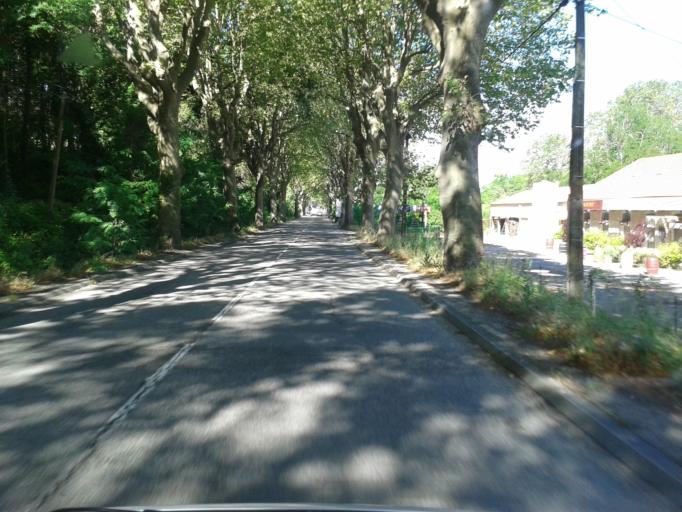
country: FR
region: Provence-Alpes-Cote d'Azur
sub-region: Departement des Bouches-du-Rhone
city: Meyrargues
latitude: 43.6431
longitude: 5.5393
